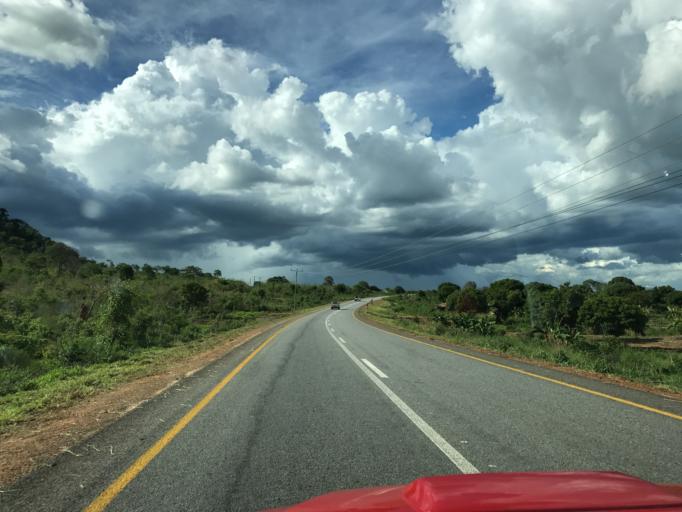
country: MZ
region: Nampula
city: Nampula
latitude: -14.9283
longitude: 38.7815
